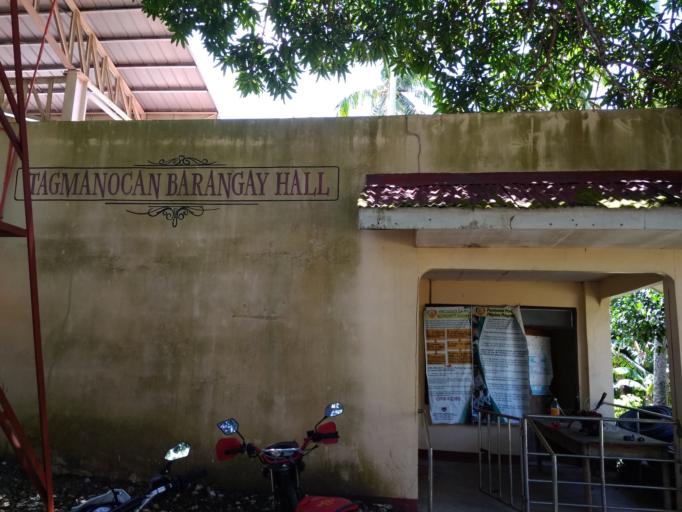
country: PH
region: Central Visayas
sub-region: Province of Siquijor
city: Lazi
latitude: 9.1463
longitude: 123.6313
